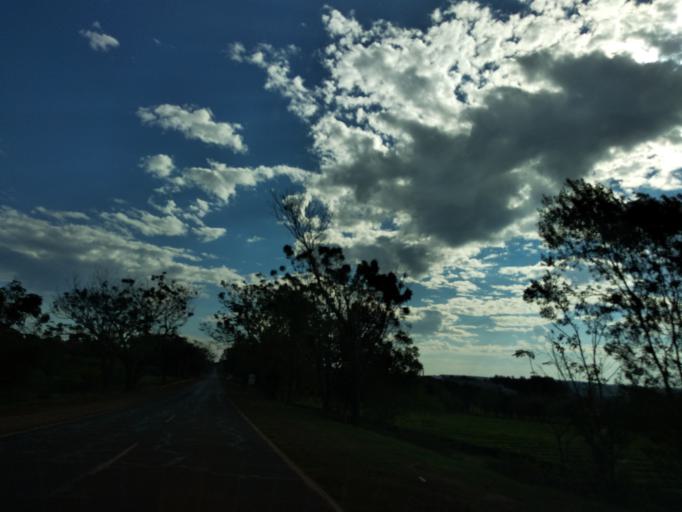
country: AR
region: Misiones
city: Jardin America
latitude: -27.0364
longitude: -55.2133
